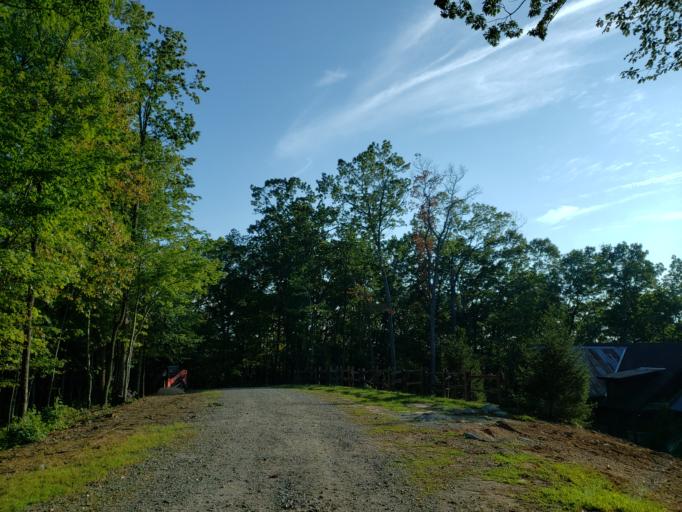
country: US
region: Georgia
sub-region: Fannin County
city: Blue Ridge
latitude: 34.6914
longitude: -84.2779
